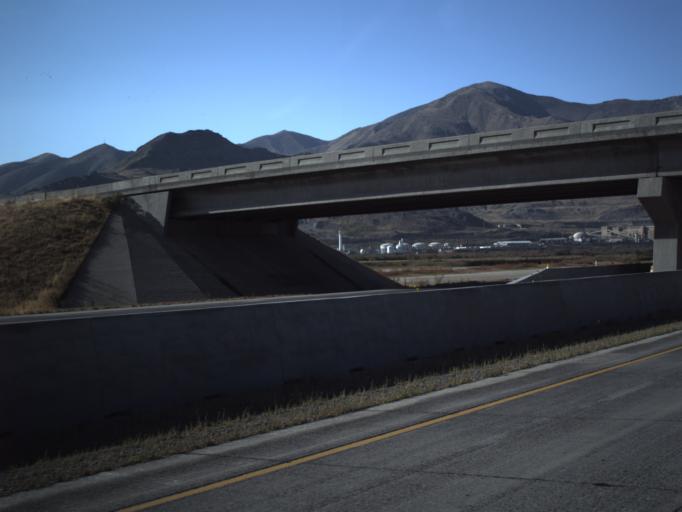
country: US
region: Utah
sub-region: Salt Lake County
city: Magna
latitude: 40.7453
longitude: -112.1833
